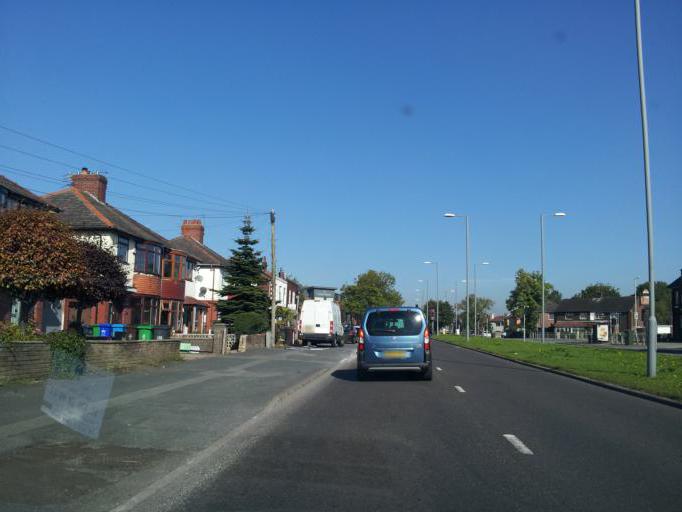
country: GB
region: England
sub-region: Manchester
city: Failsworth
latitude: 53.5160
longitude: -2.1695
